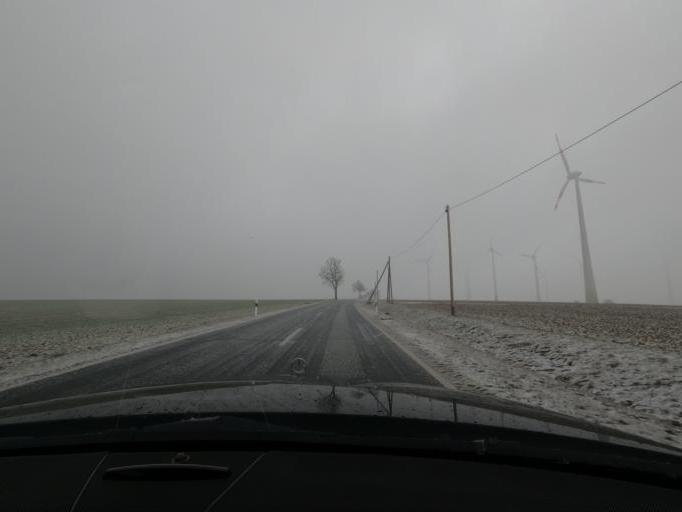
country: DE
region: Thuringia
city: Buttstedt
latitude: 51.2331
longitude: 10.2938
